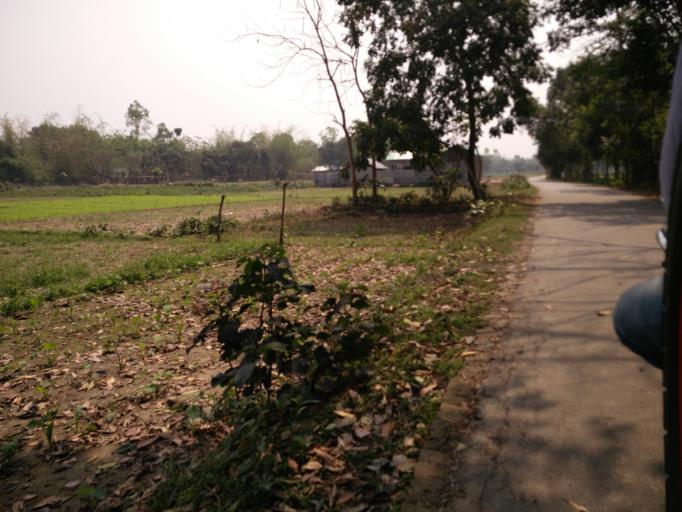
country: BD
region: Dhaka
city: Muktagacha
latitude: 24.8909
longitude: 90.2680
